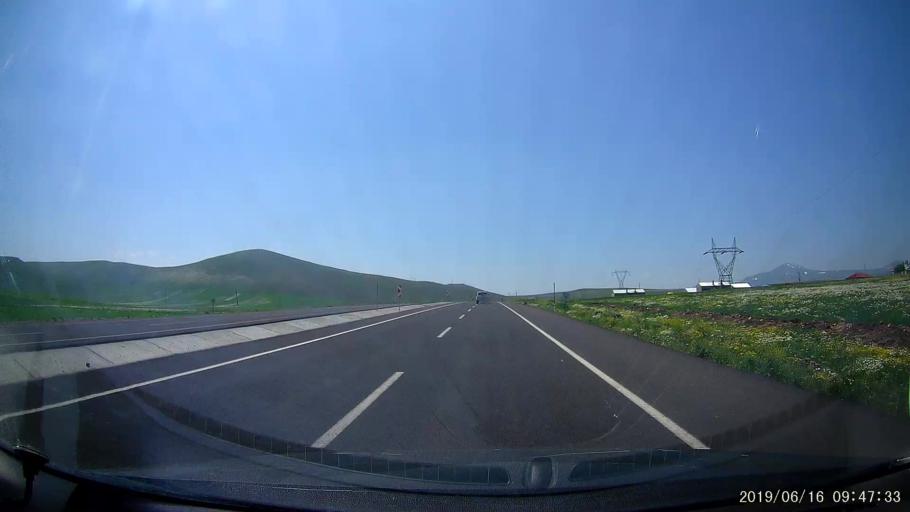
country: TR
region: Kars
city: Digor
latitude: 40.4453
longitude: 43.3453
